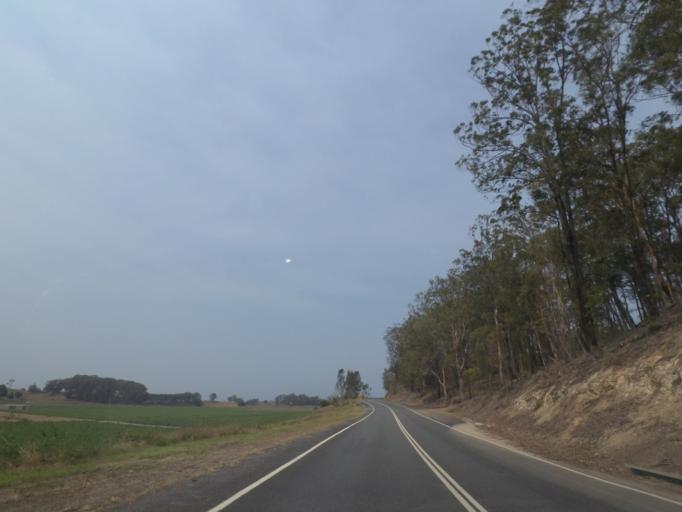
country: AU
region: New South Wales
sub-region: Tweed
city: Burringbar
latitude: -28.4584
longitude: 153.5196
